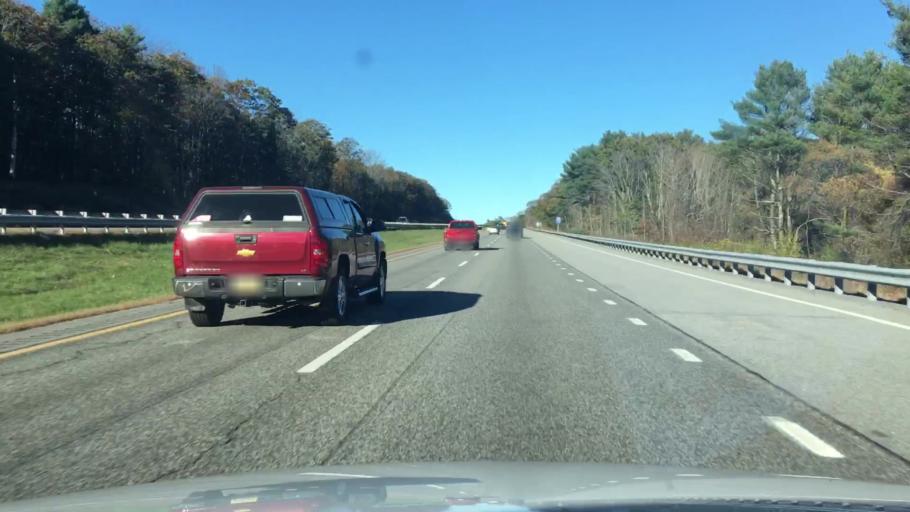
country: US
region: Maine
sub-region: Cumberland County
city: Freeport
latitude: 43.8796
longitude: -70.0842
